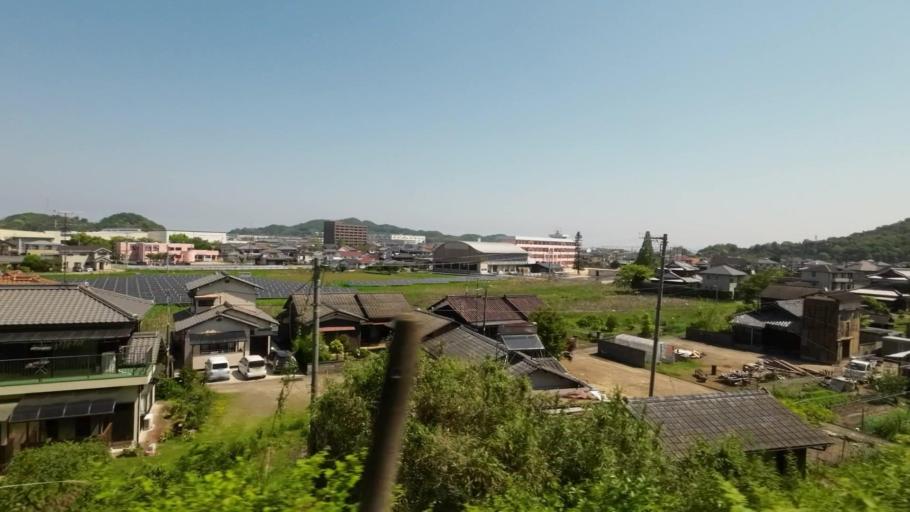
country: JP
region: Ehime
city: Niihama
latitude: 33.9727
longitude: 133.3495
